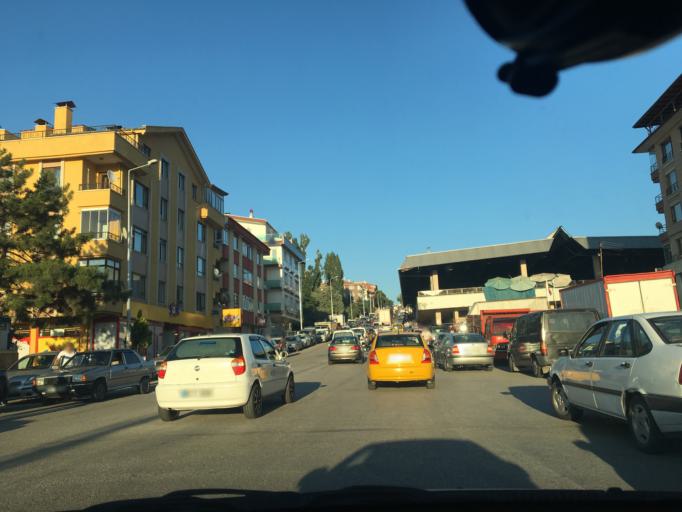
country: TR
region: Ankara
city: Ankara
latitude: 39.8837
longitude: 32.8315
